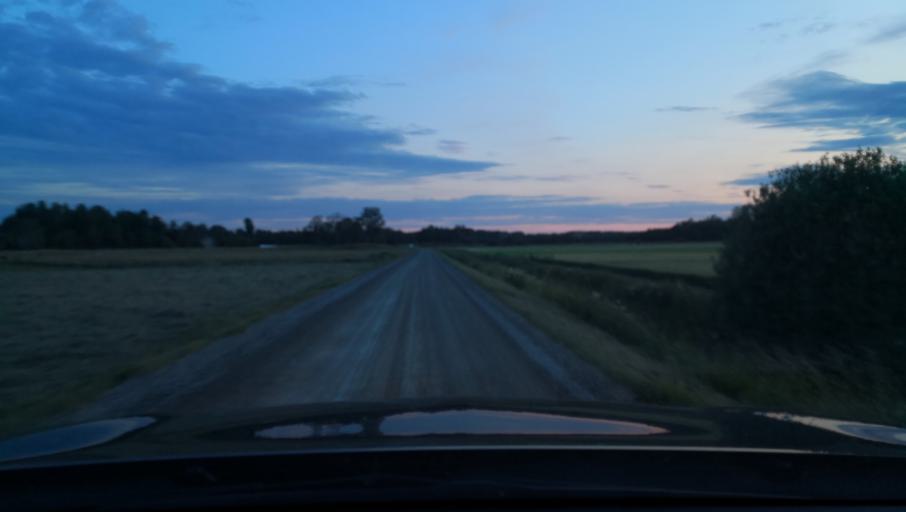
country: SE
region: Uppsala
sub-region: Osthammars Kommun
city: Bjorklinge
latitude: 60.0082
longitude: 17.4071
